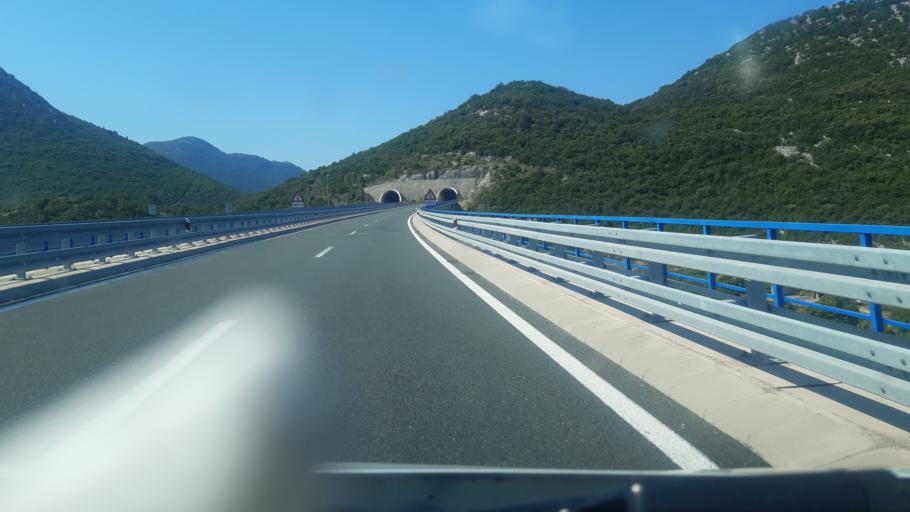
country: HR
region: Dubrovacko-Neretvanska
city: Komin
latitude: 43.1186
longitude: 17.4831
